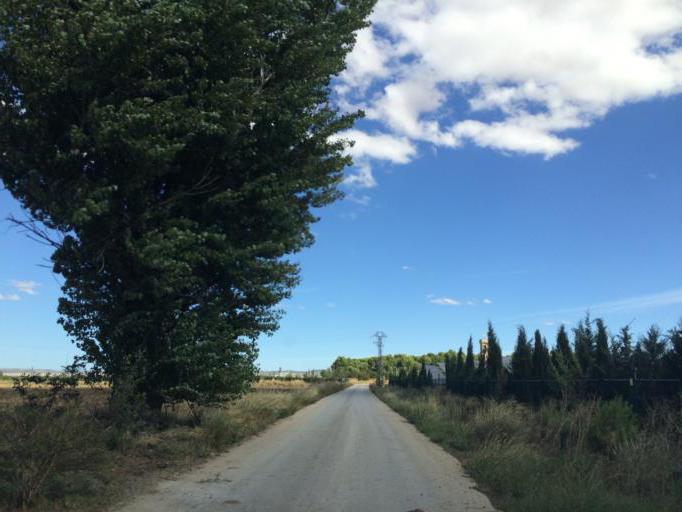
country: ES
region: Castille-La Mancha
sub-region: Provincia de Albacete
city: Albacete
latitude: 38.9296
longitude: -1.8666
